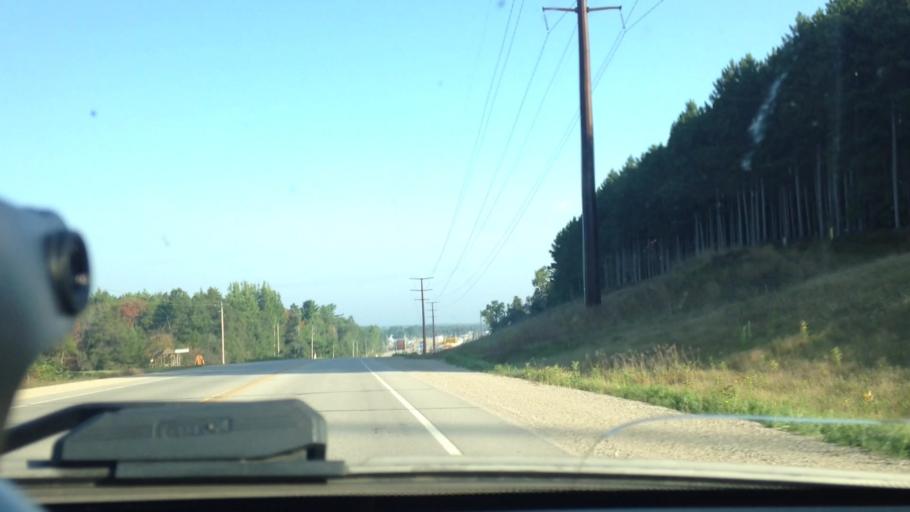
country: US
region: Wisconsin
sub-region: Marinette County
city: Peshtigo
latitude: 45.2139
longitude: -87.9957
